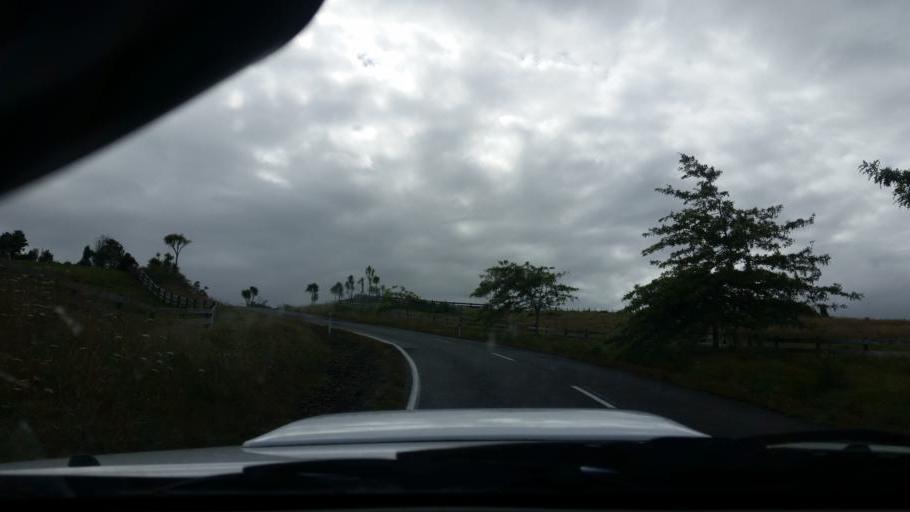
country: NZ
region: Auckland
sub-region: Auckland
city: Wellsford
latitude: -36.1318
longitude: 174.3631
